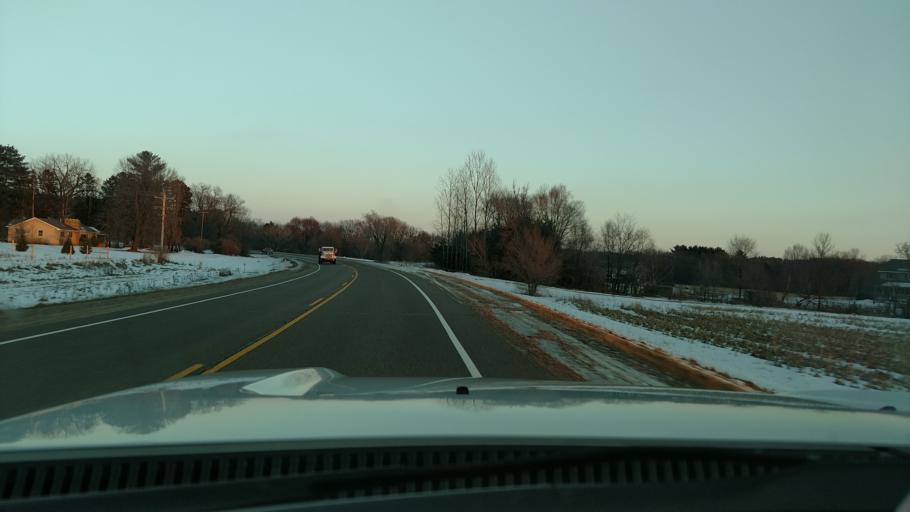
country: US
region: Wisconsin
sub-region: Pierce County
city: River Falls
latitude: 44.8982
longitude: -92.5899
